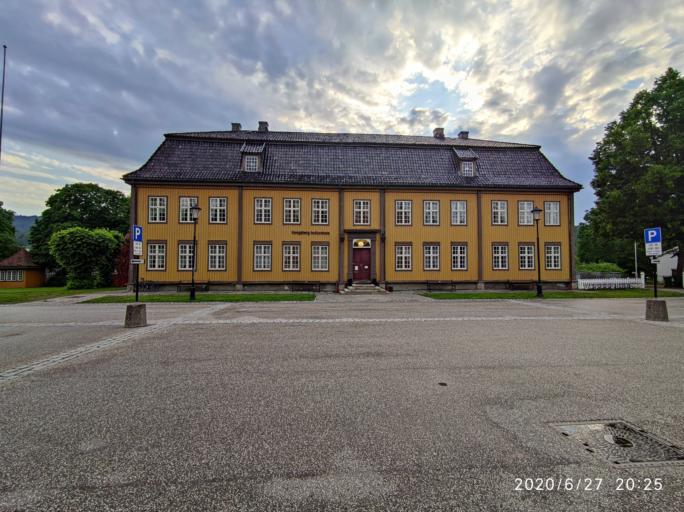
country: NO
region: Buskerud
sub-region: Kongsberg
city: Kongsberg
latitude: 59.6658
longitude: 9.6458
